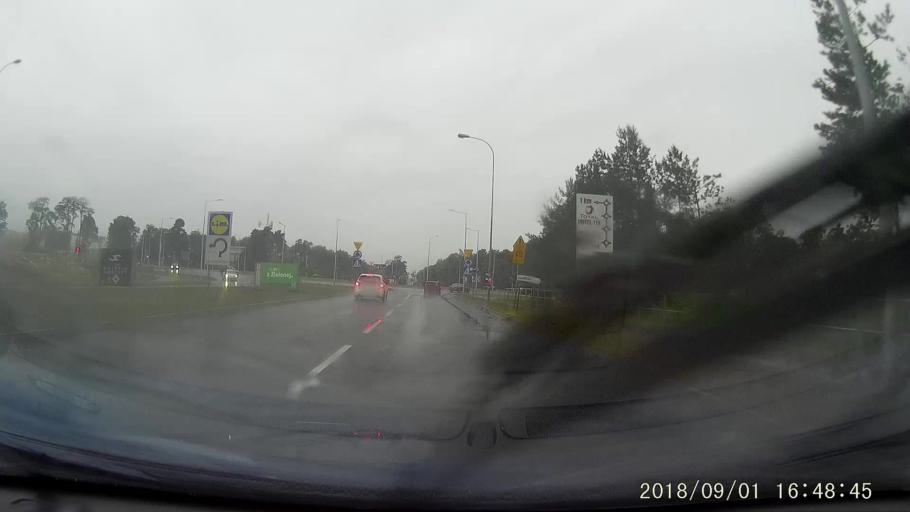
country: PL
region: Lubusz
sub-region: Zielona Gora
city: Zielona Gora
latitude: 51.9584
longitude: 15.5271
